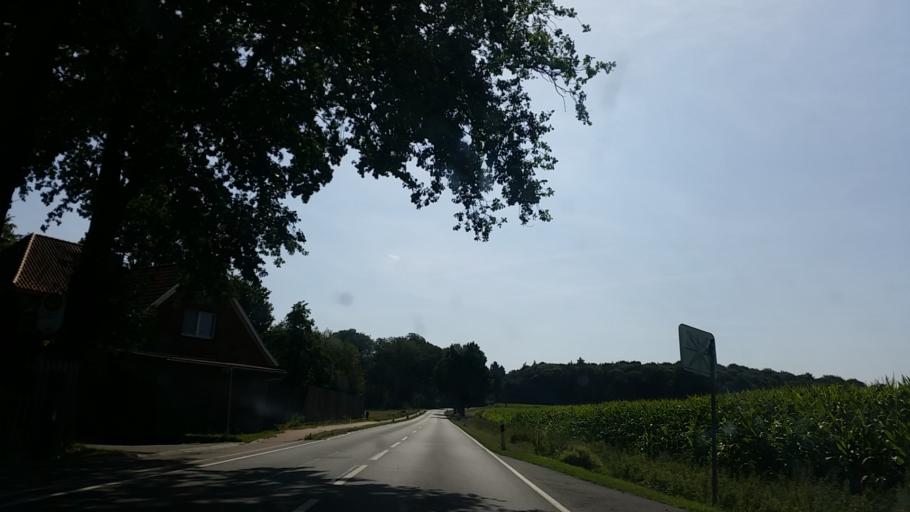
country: DE
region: Lower Saxony
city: Ankum
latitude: 52.5268
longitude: 7.8954
